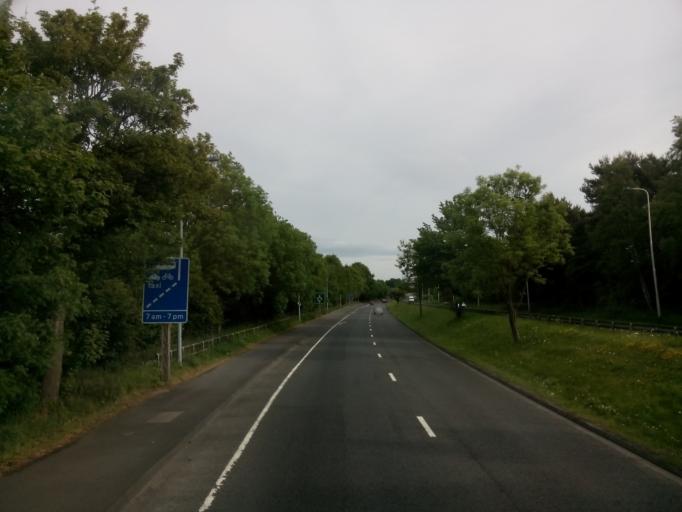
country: GB
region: England
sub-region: County Durham
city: Sacriston
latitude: 54.8133
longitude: -1.5897
